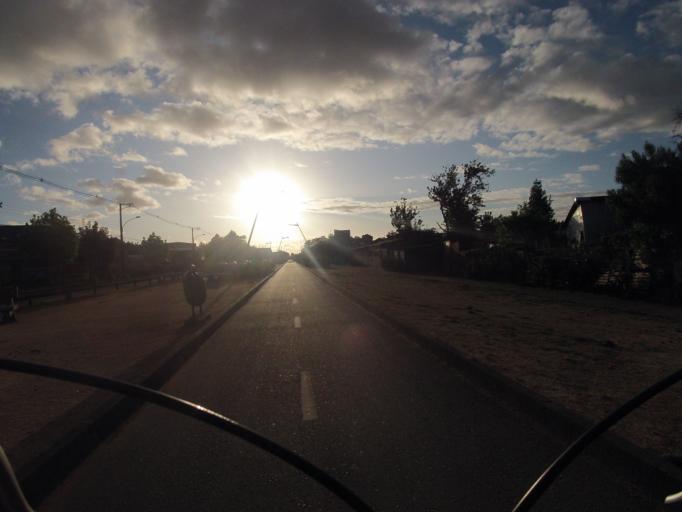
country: CL
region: Araucania
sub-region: Provincia de Cautin
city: Temuco
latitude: -38.7444
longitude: -72.6142
